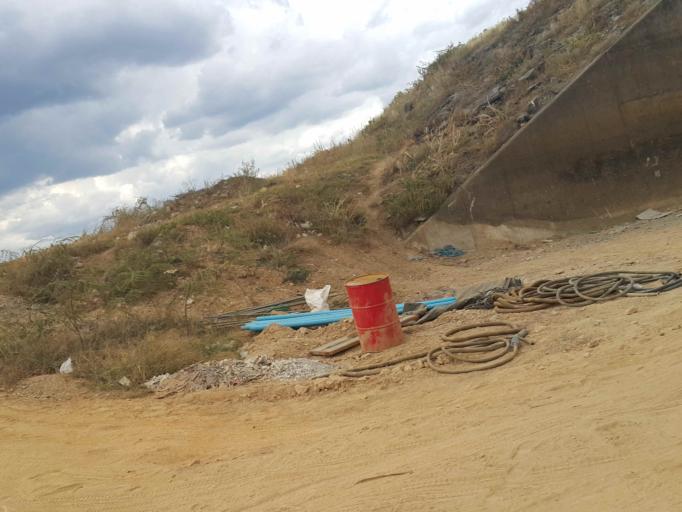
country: TH
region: Sukhothai
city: Thung Saliam
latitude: 17.3111
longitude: 99.4252
